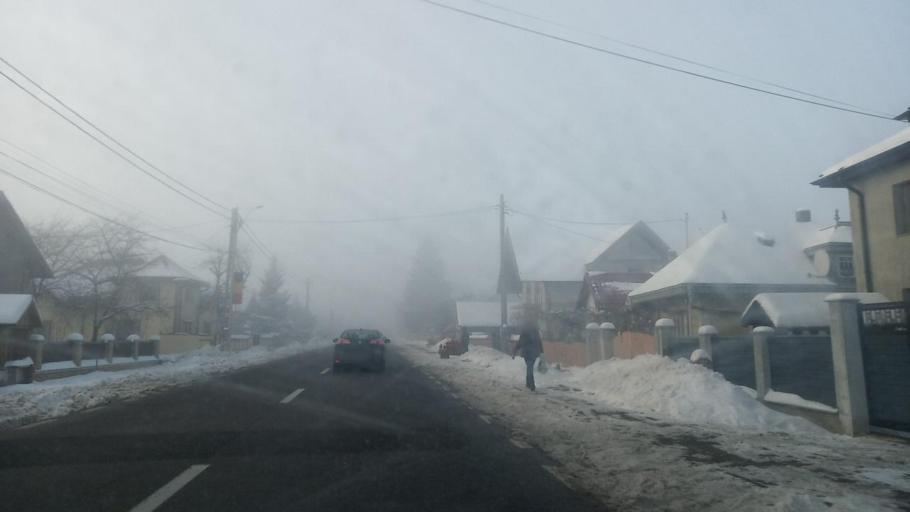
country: RO
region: Suceava
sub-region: Comuna Cornu Luncii
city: Braiesti
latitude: 47.5034
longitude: 26.0538
